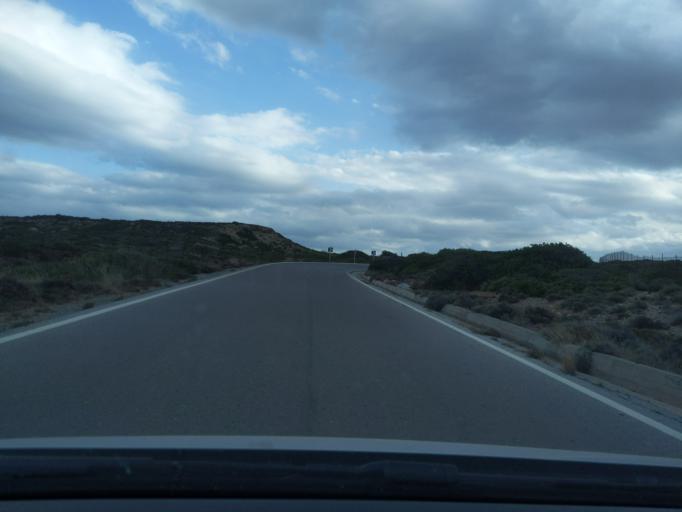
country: GR
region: Crete
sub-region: Nomos Lasithiou
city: Palekastro
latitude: 35.2429
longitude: 26.2488
